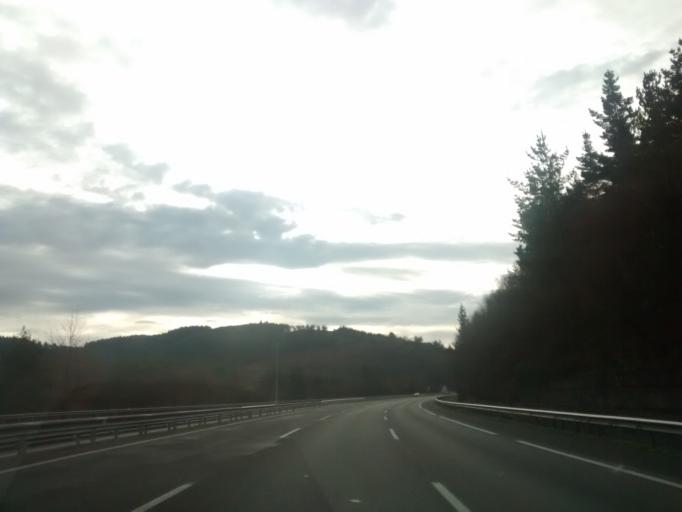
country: ES
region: Basque Country
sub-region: Provincia de Alava
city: Lezama
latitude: 43.0507
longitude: -2.9264
